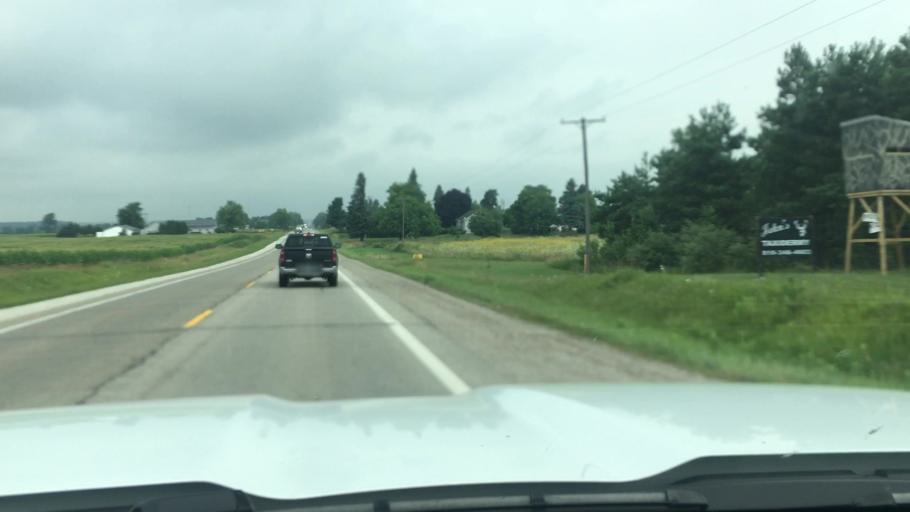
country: US
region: Michigan
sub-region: Sanilac County
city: Brown City
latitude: 43.1911
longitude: -83.0766
